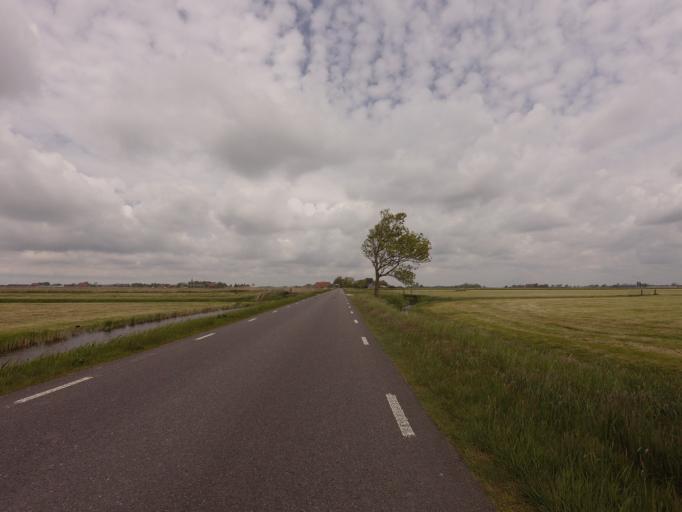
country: NL
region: Friesland
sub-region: Sudwest Fryslan
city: Bolsward
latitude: 53.1008
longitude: 5.5378
